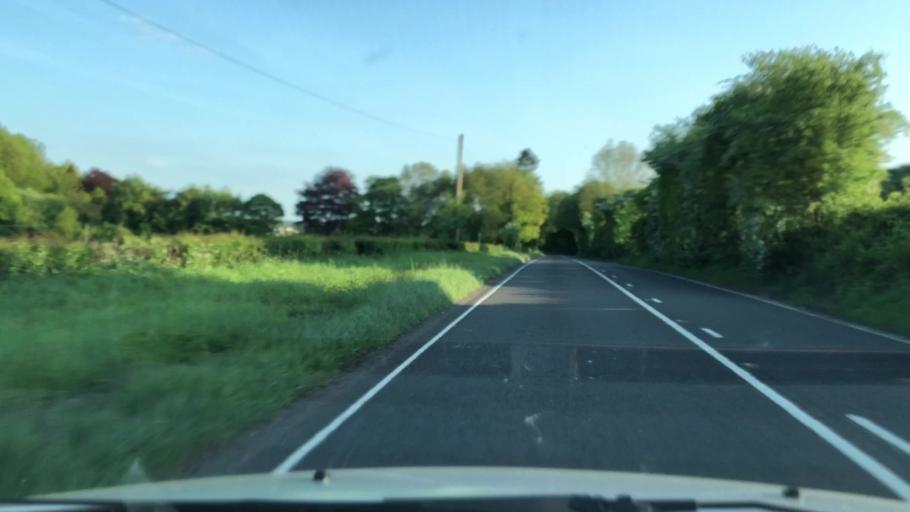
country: GB
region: England
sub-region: Hampshire
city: Alton
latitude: 51.1620
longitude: -0.9899
